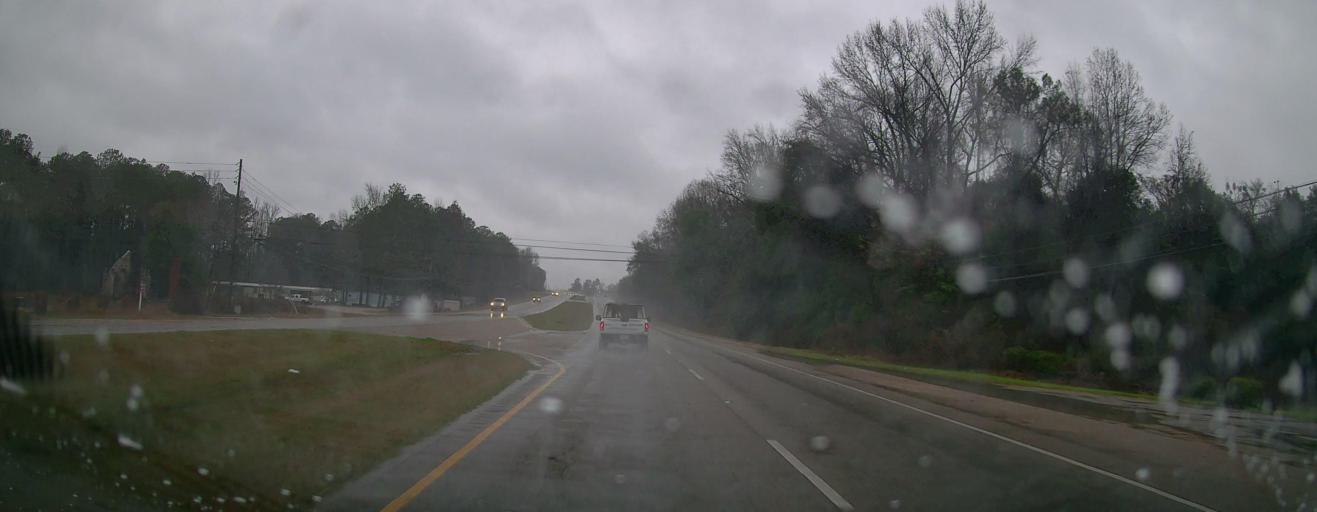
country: US
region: Alabama
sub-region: Autauga County
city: Prattville
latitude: 32.4277
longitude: -86.4129
